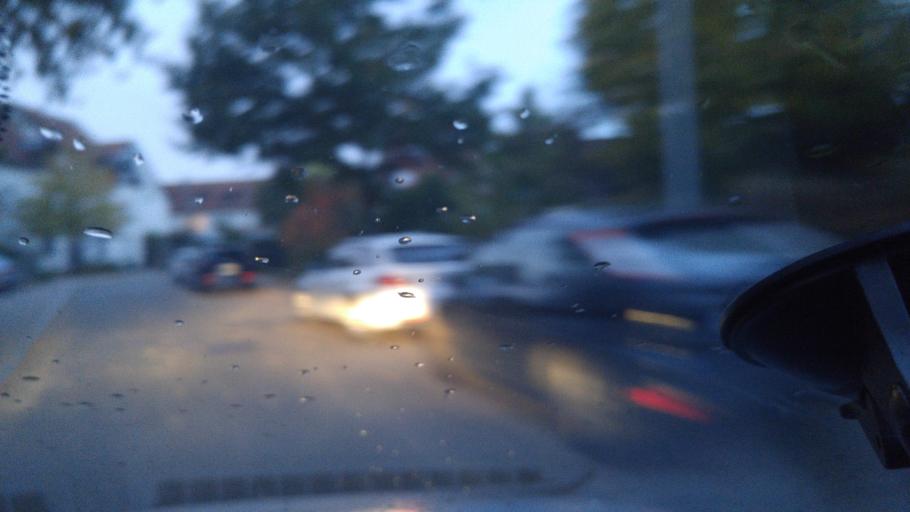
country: DE
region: Baden-Wuerttemberg
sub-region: Regierungsbezirk Stuttgart
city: Ditzingen
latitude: 48.8300
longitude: 9.0783
